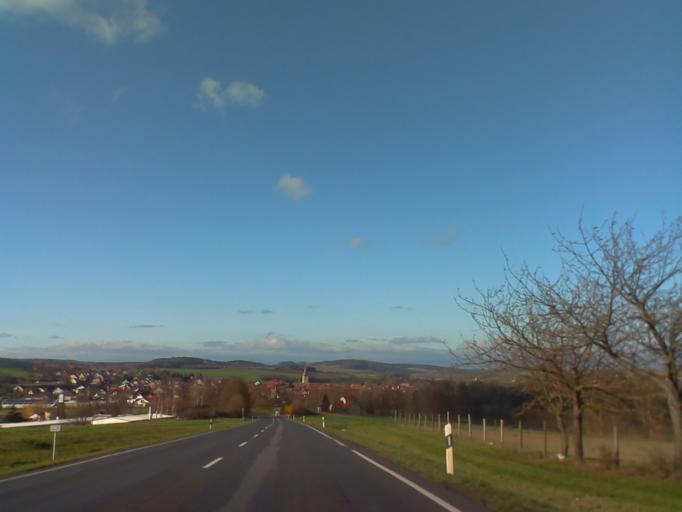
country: DE
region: Bavaria
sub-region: Regierungsbezirk Unterfranken
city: Saal an der Saale
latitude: 50.3135
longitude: 10.3730
